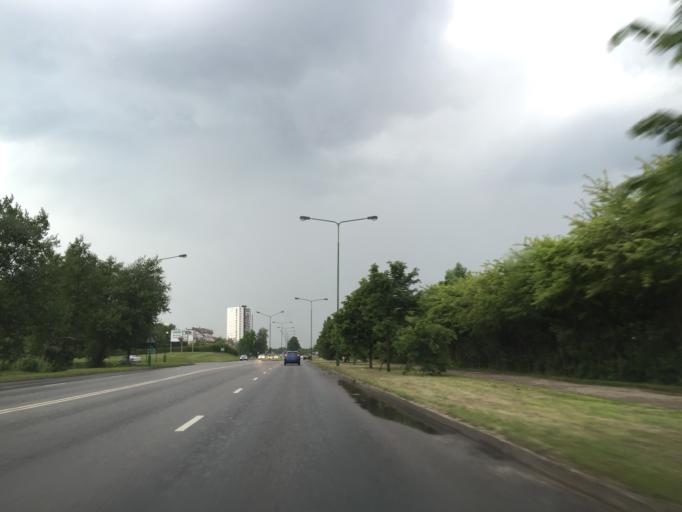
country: LT
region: Klaipedos apskritis
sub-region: Klaipeda
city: Klaipeda
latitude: 55.7425
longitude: 21.1303
